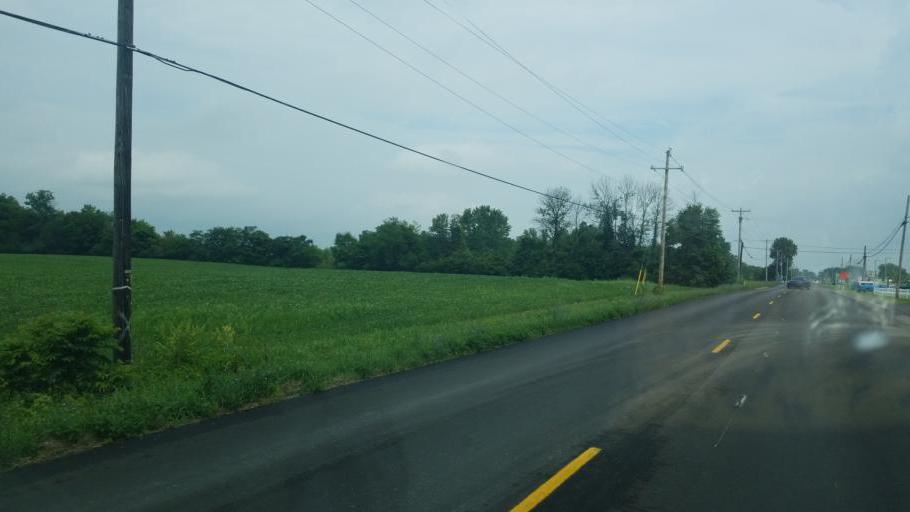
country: US
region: Ohio
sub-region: Logan County
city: Russells Point
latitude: 40.4696
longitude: -83.8600
